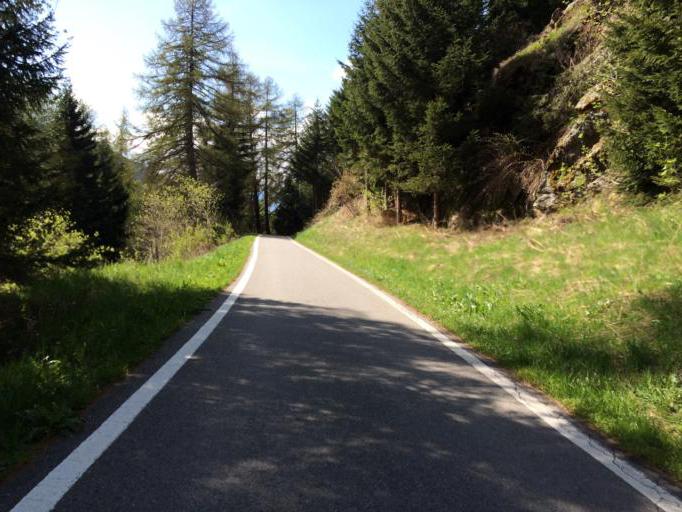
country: IT
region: Trentino-Alto Adige
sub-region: Bolzano
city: Malles Venosta
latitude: 46.7375
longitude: 10.5330
